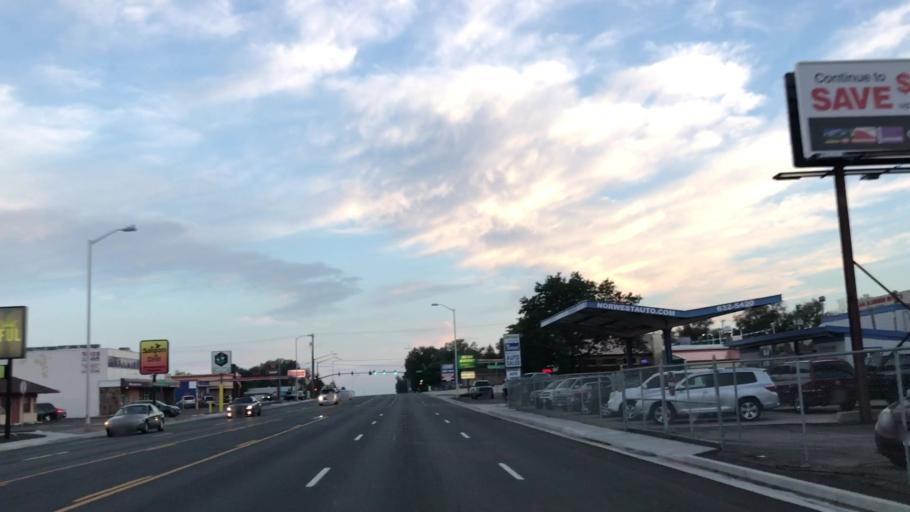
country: US
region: Colorado
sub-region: El Paso County
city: Colorado Springs
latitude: 38.8378
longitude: -104.7760
